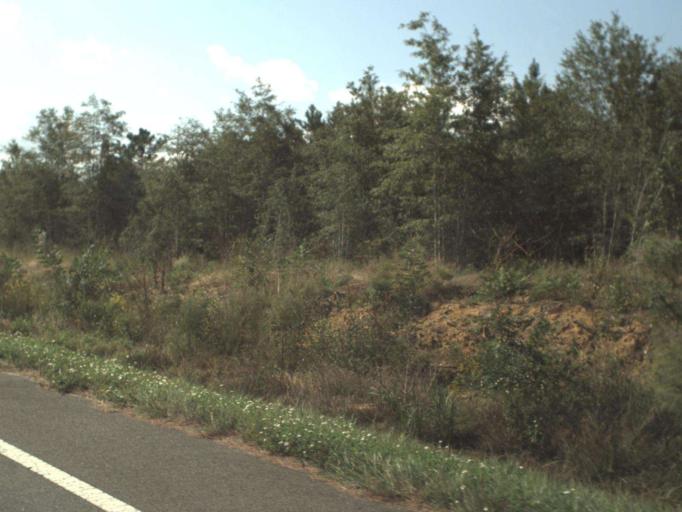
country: US
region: Florida
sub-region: Holmes County
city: Bonifay
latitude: 30.5999
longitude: -85.7661
